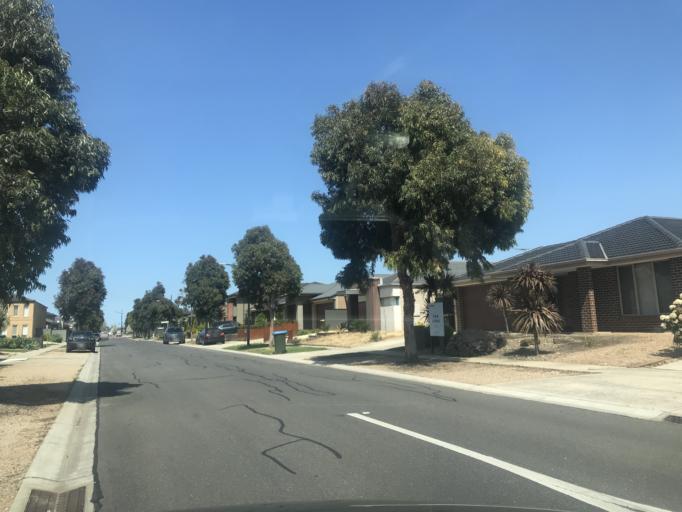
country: AU
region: Victoria
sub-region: Wyndham
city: Hoppers Crossing
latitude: -37.8838
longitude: 144.7221
